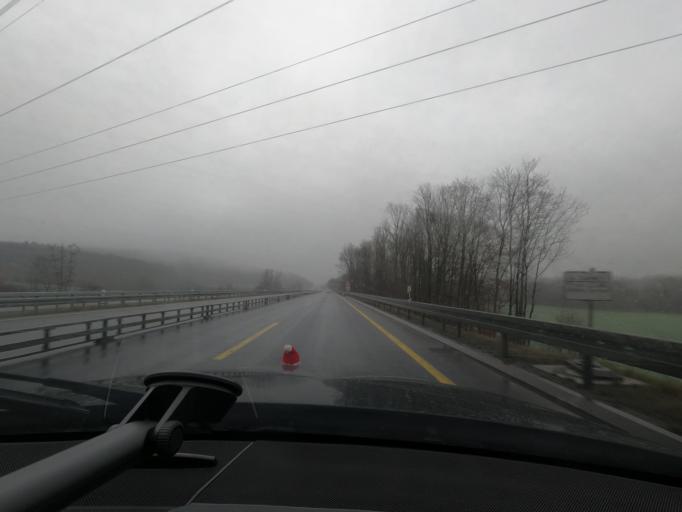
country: DE
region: Lower Saxony
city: Seesen
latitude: 51.8607
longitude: 10.1259
